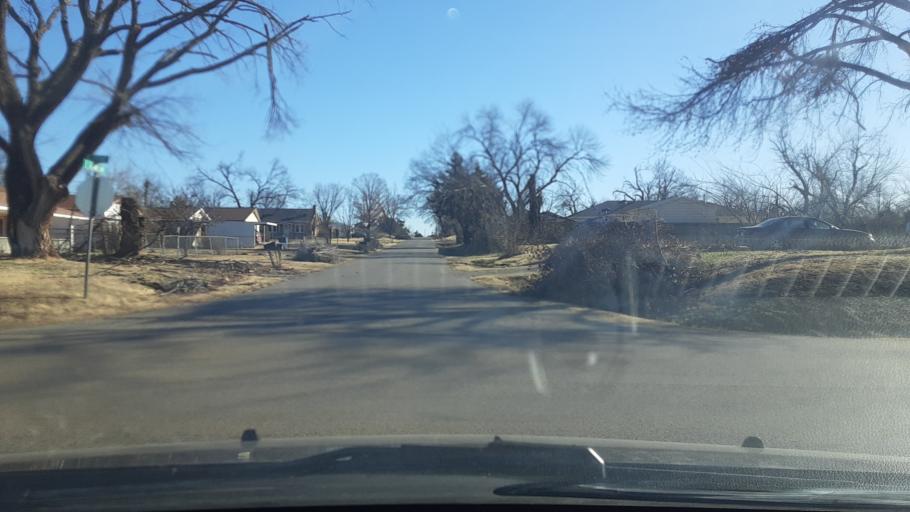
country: US
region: Oklahoma
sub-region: Logan County
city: Guthrie
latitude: 35.8729
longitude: -97.4076
